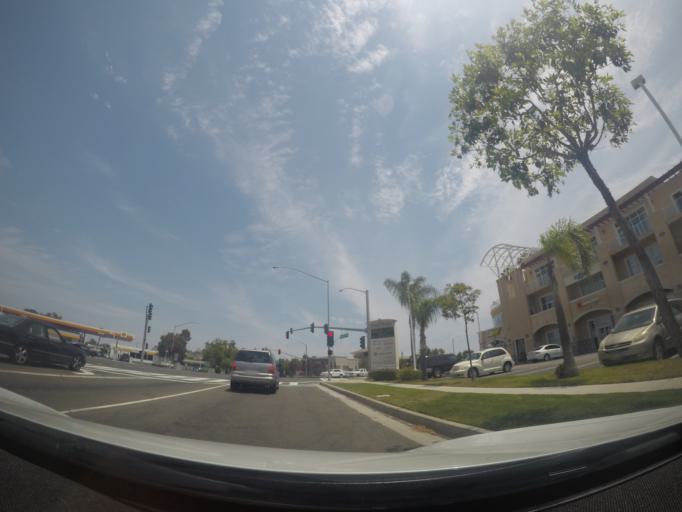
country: US
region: California
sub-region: Los Angeles County
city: Torrance
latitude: 33.8161
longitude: -118.3516
